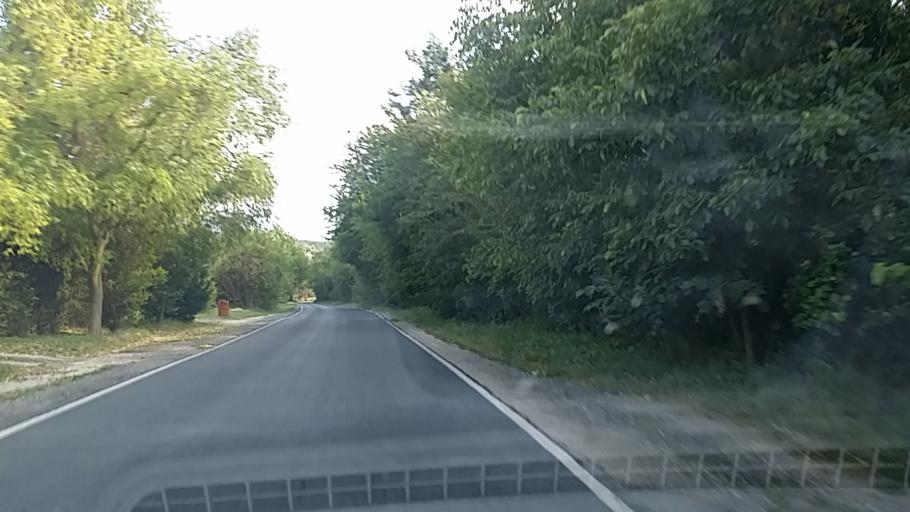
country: HU
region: Gyor-Moson-Sopron
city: Fertorakos
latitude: 47.7288
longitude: 16.6222
